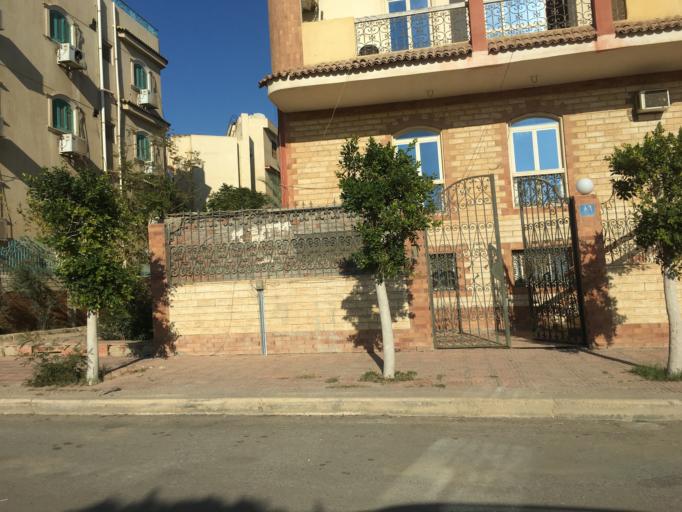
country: EG
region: Al Jizah
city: Madinat Sittah Uktubar
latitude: 29.9871
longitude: 30.9422
